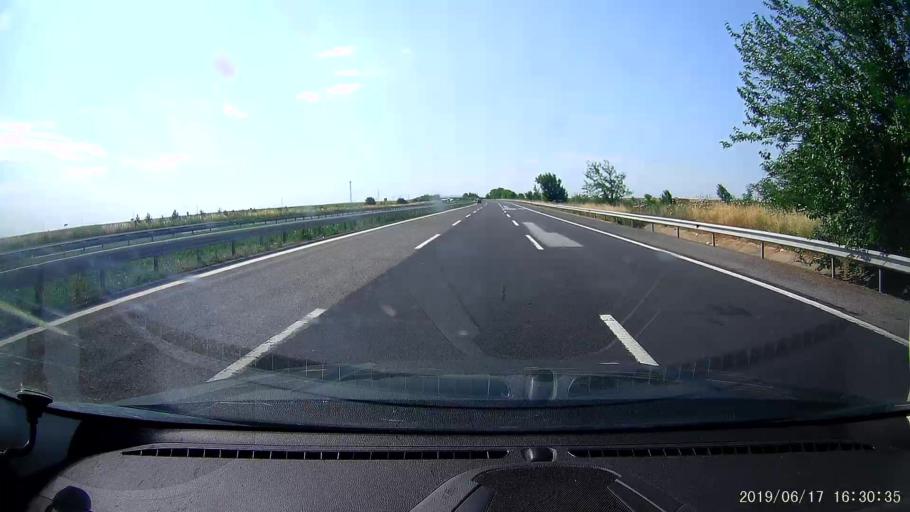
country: TR
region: Tekirdag
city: Beyazkoy
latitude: 41.3493
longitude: 27.6501
